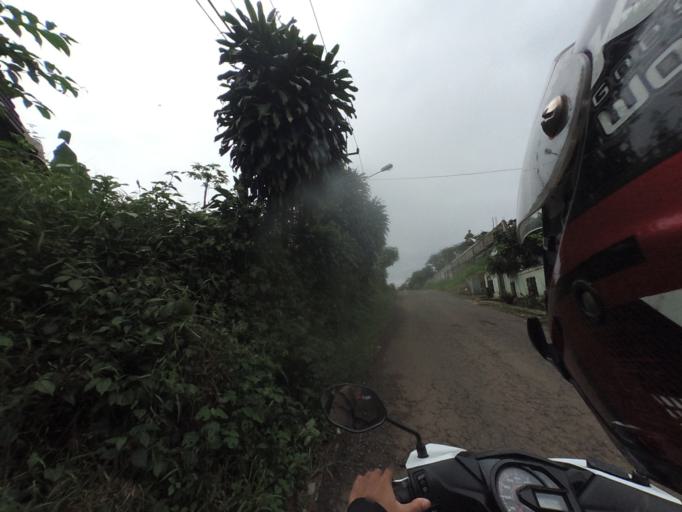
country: ID
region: West Java
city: Bogor
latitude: -6.6387
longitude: 106.7390
